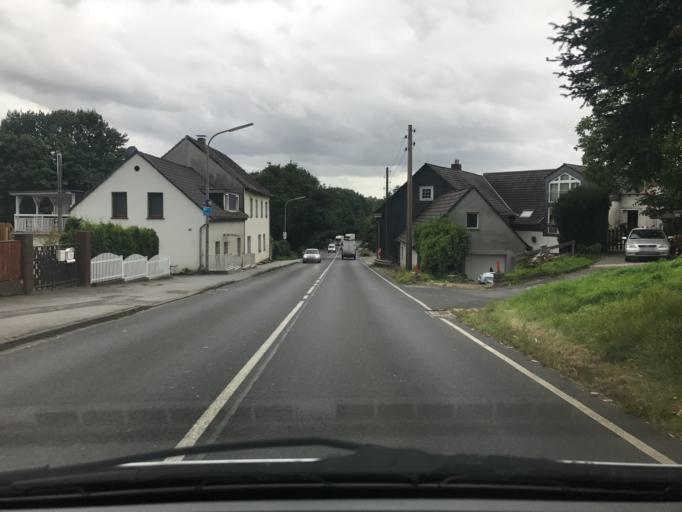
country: DE
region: North Rhine-Westphalia
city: Haan
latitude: 51.2070
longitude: 7.0294
